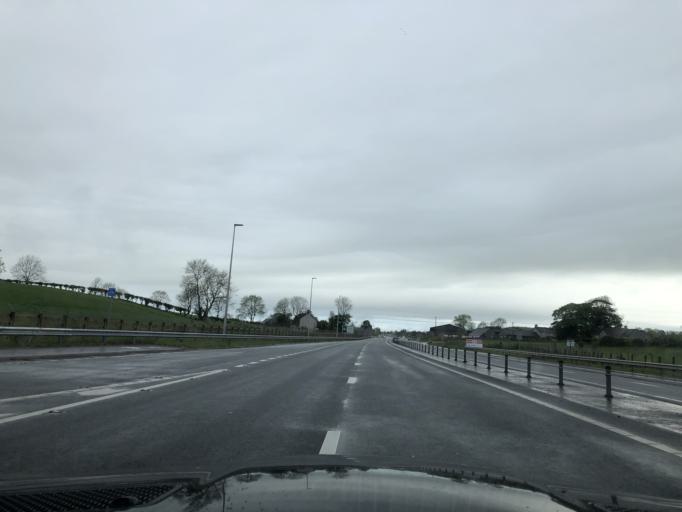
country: GB
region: Northern Ireland
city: Dunloy
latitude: 55.0053
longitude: -6.3598
